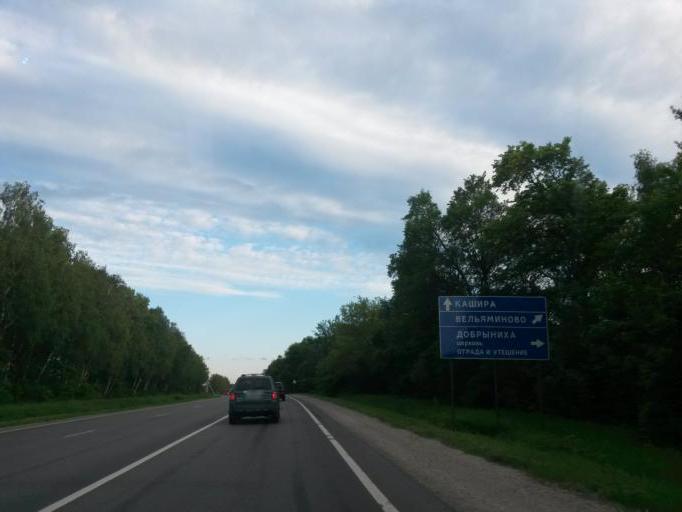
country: RU
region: Moskovskaya
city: Barybino
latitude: 55.2073
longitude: 37.8684
